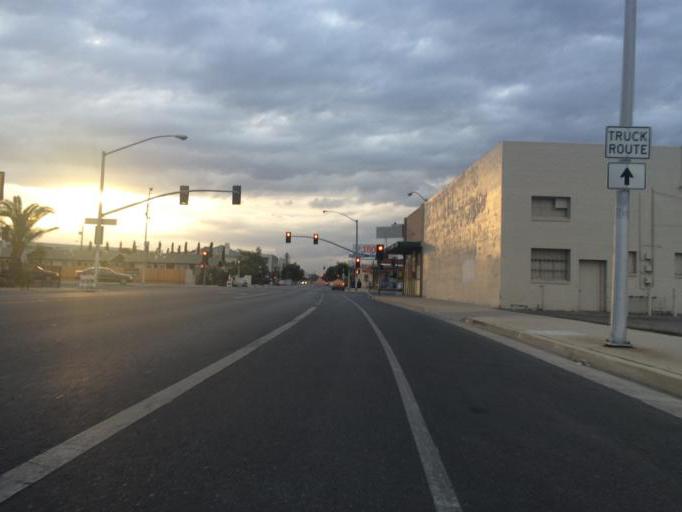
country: US
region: California
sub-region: Fresno County
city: Fresno
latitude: 36.7437
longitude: -119.7981
